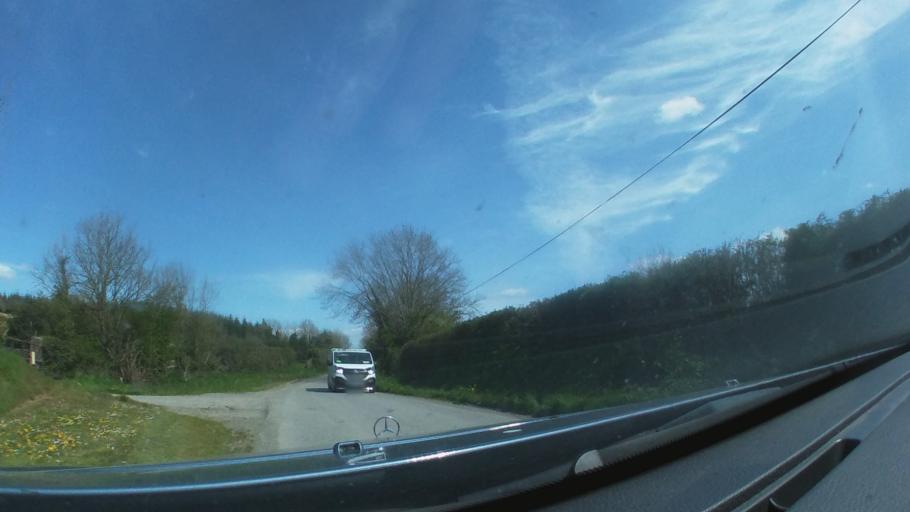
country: IE
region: Leinster
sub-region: Kilkenny
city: Callan
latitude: 52.6232
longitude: -7.4677
